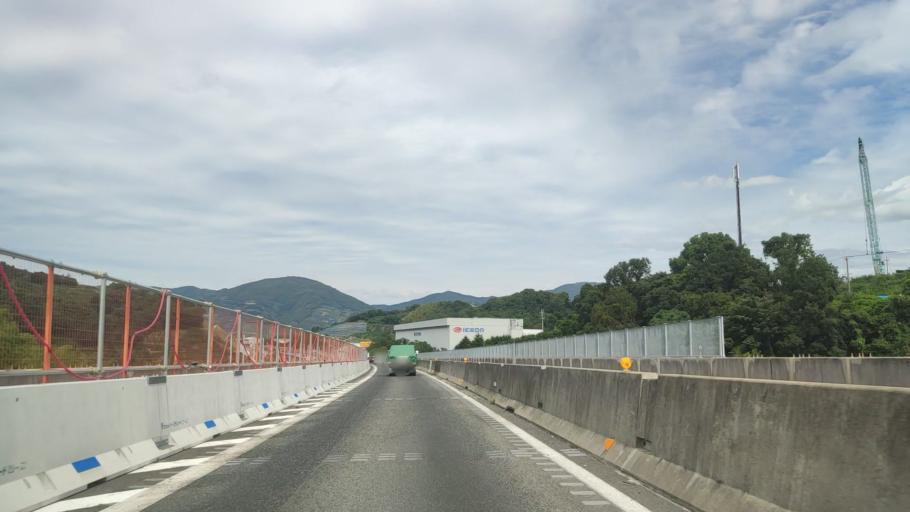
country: JP
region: Wakayama
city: Kainan
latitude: 34.0424
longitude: 135.2035
